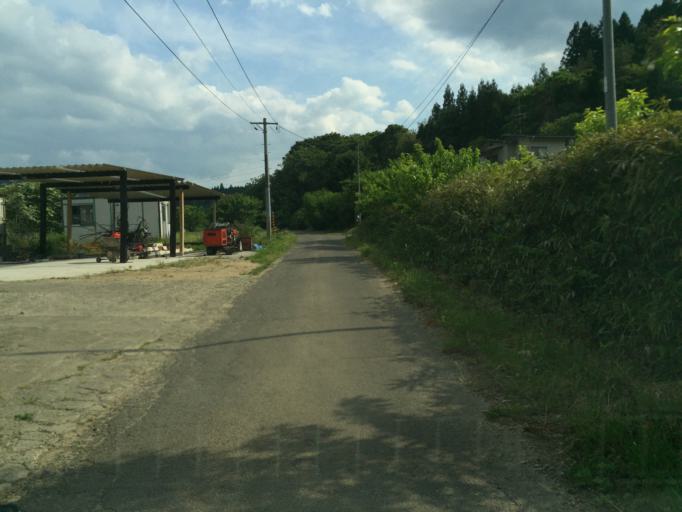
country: JP
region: Fukushima
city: Fukushima-shi
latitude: 37.7091
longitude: 140.3471
